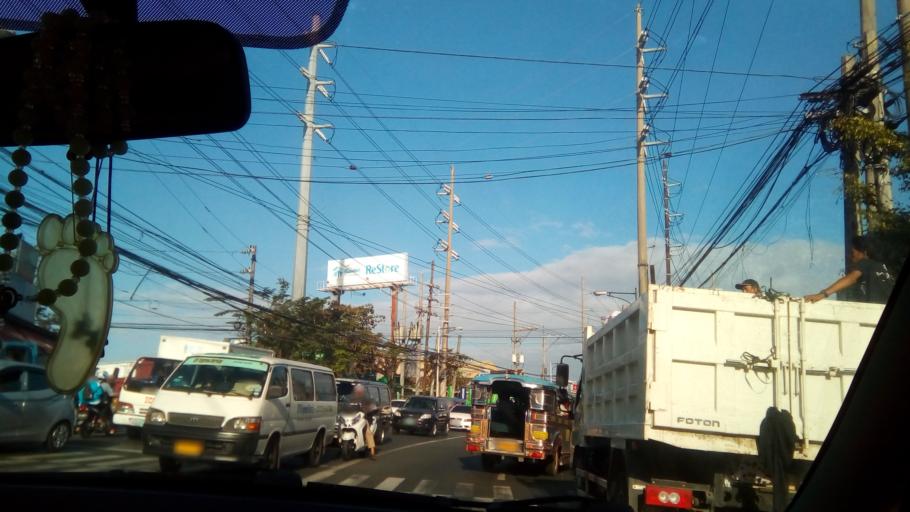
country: PH
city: Sambayanihan People's Village
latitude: 14.4225
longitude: 121.0228
